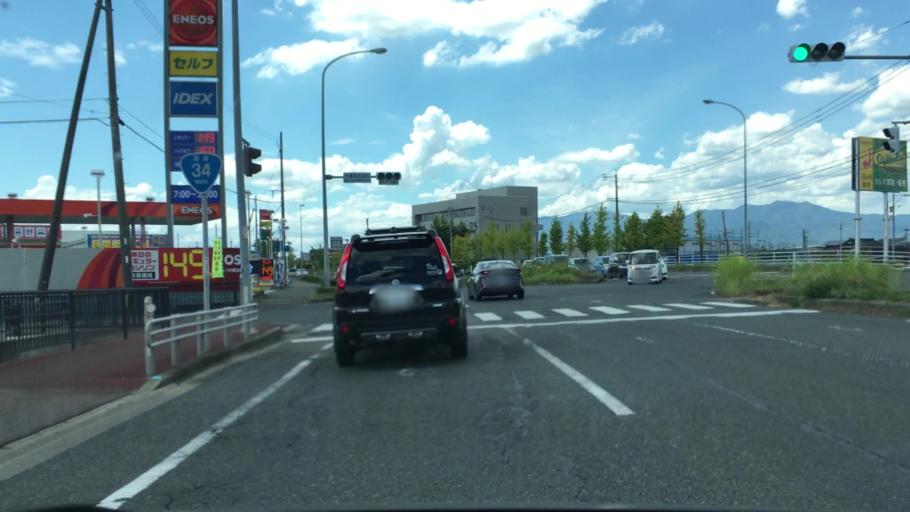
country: JP
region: Saga Prefecture
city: Saga-shi
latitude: 33.2770
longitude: 130.3119
